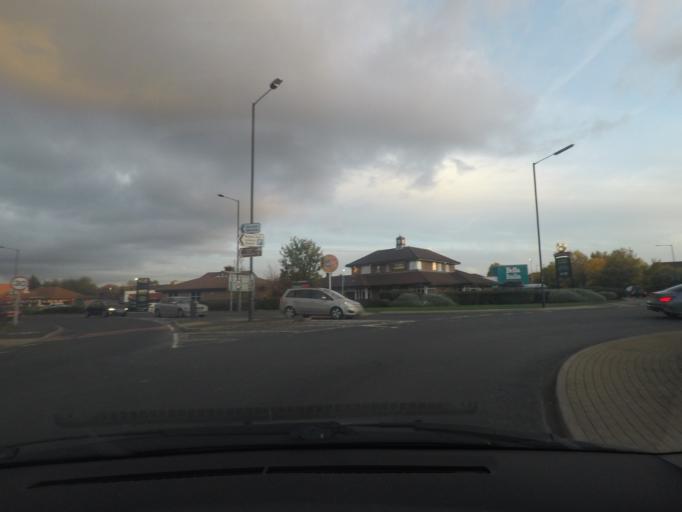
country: GB
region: England
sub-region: City of York
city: Skelton
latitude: 53.9903
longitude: -1.1053
